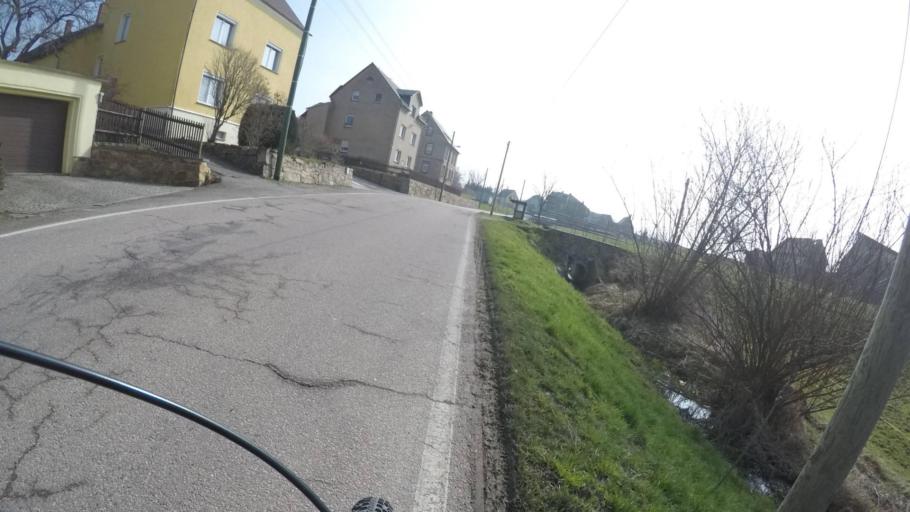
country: DE
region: Saxony
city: Niederfrohna
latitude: 50.8876
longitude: 12.6898
